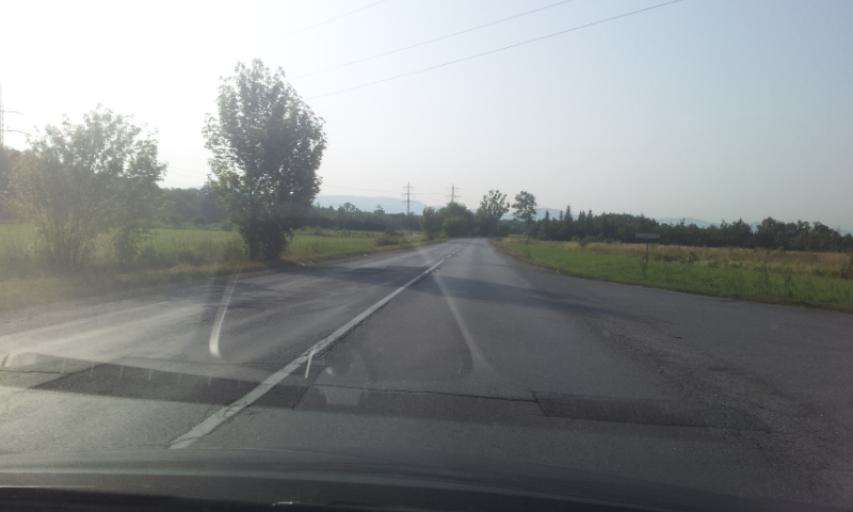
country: SK
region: Kosicky
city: Kosice
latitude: 48.6407
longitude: 21.2024
